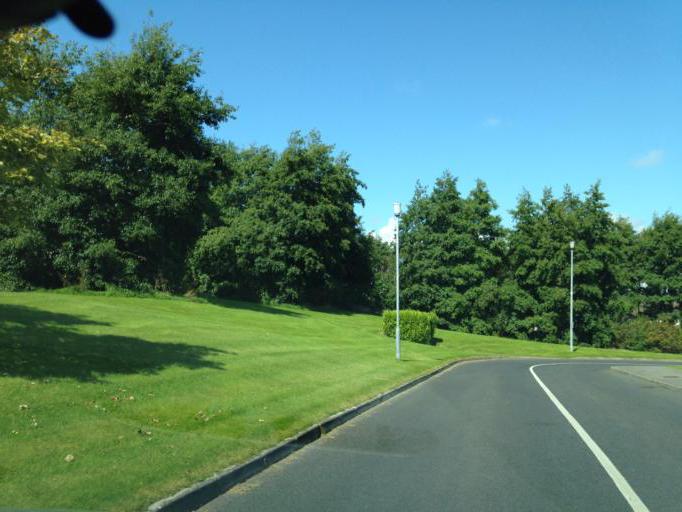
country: IE
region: Connaught
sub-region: County Galway
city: Gaillimh
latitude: 53.2695
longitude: -9.0886
